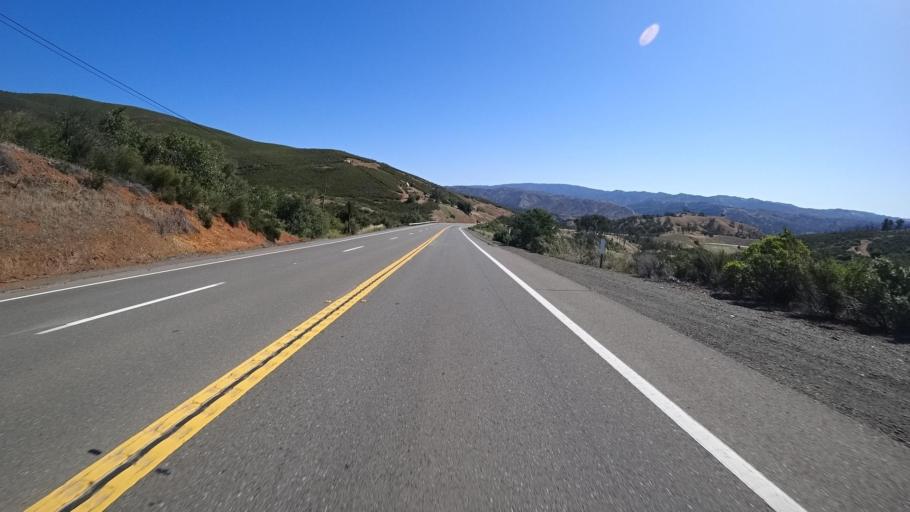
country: US
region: California
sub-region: Lake County
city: Clearlake
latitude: 39.0158
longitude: -122.6006
